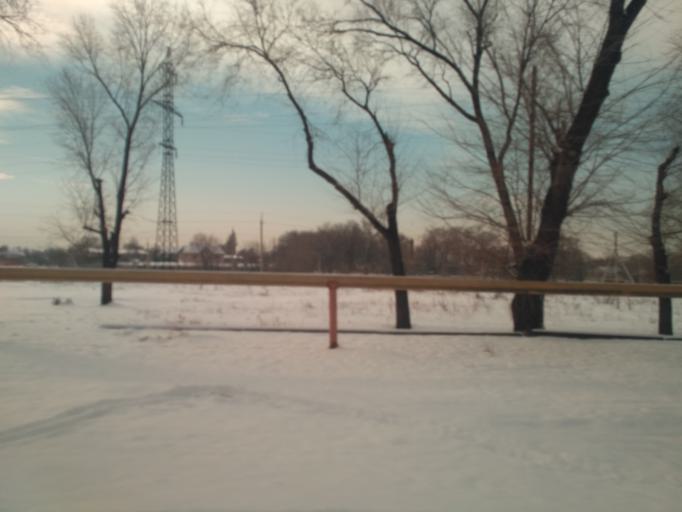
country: KZ
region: Almaty Qalasy
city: Almaty
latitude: 43.2161
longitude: 76.7720
